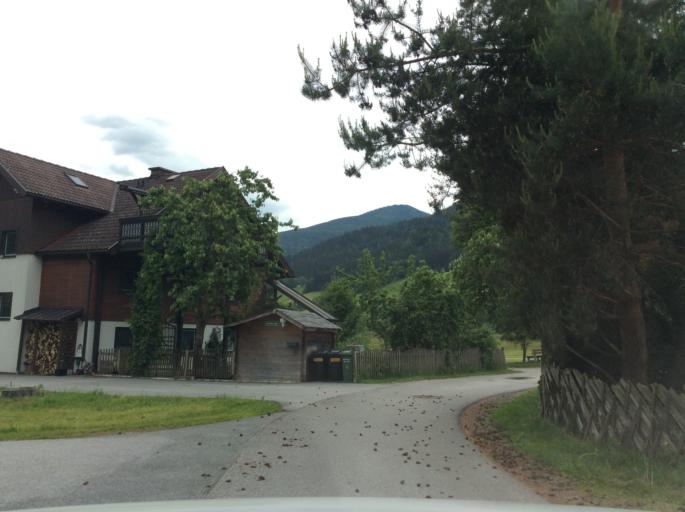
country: AT
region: Styria
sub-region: Politischer Bezirk Liezen
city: Schladming
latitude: 47.4042
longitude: 13.7094
